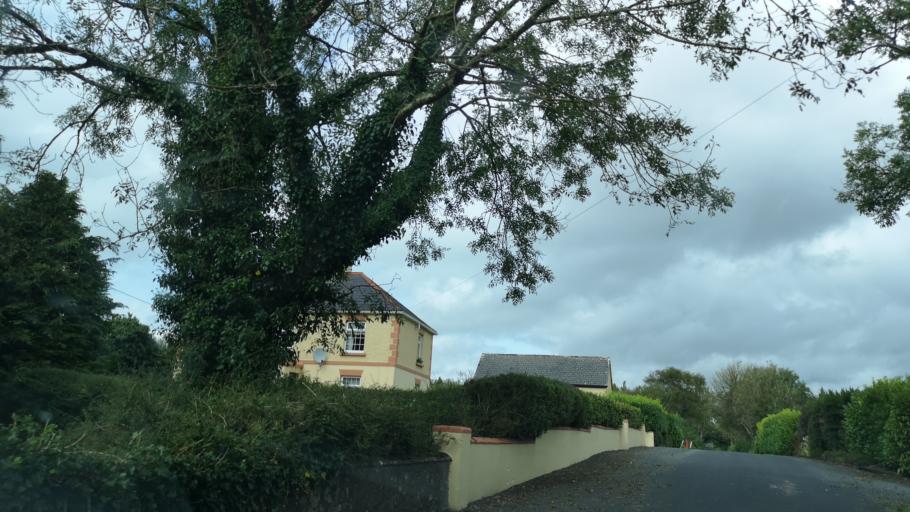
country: IE
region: Connaught
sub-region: County Galway
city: Athenry
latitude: 53.2914
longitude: -8.6635
